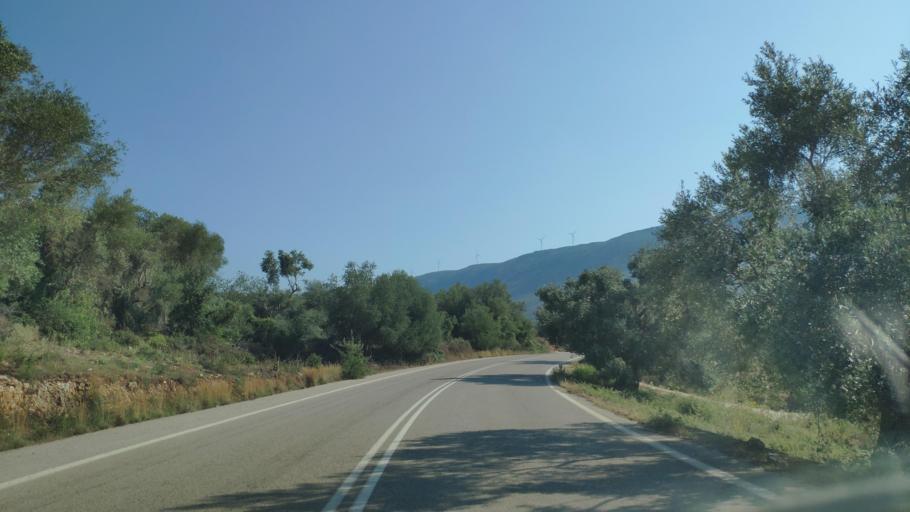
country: GR
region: West Greece
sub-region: Nomos Aitolias kai Akarnanias
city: Stanos
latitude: 38.7733
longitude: 21.1831
